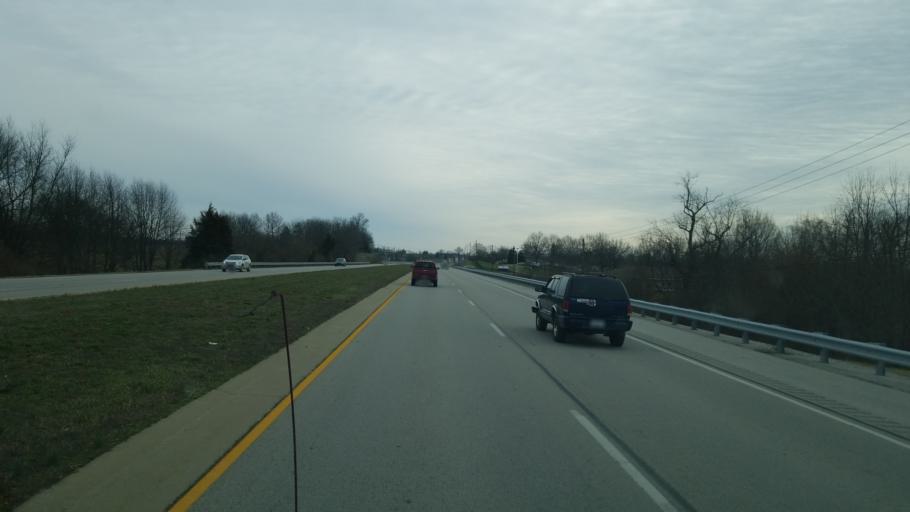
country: US
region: Kentucky
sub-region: Bourbon County
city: Paris
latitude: 38.2241
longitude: -84.2409
